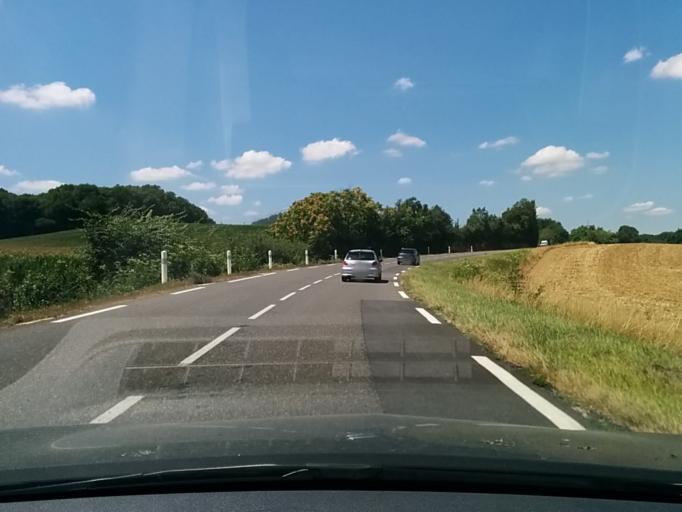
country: FR
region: Midi-Pyrenees
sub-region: Departement du Gers
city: Vic-Fezensac
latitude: 43.7436
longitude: 0.3513
